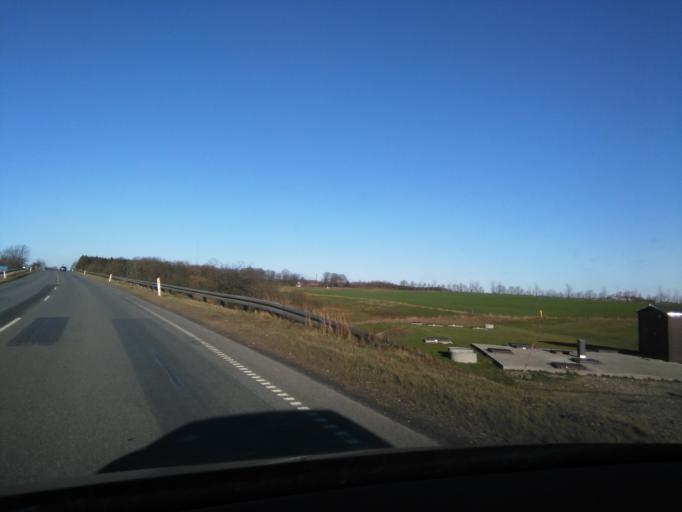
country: DK
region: North Denmark
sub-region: Mariagerfjord Kommune
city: Hobro
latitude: 56.6626
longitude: 9.8054
